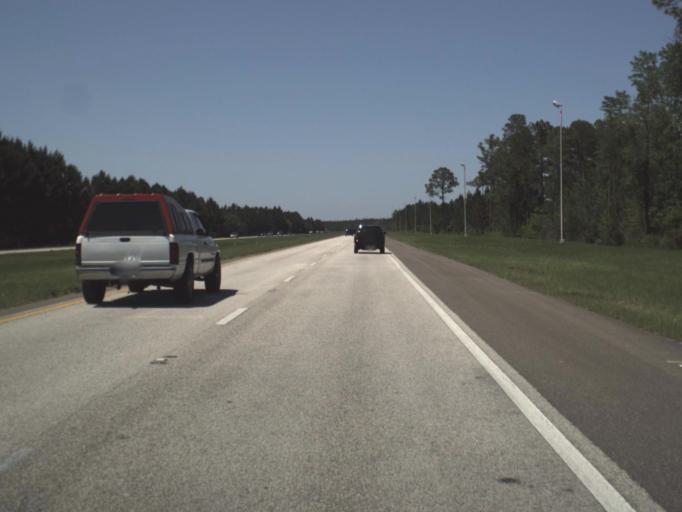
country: US
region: Florida
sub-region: Clay County
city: Bellair-Meadowbrook Terrace
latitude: 30.2042
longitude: -81.8372
